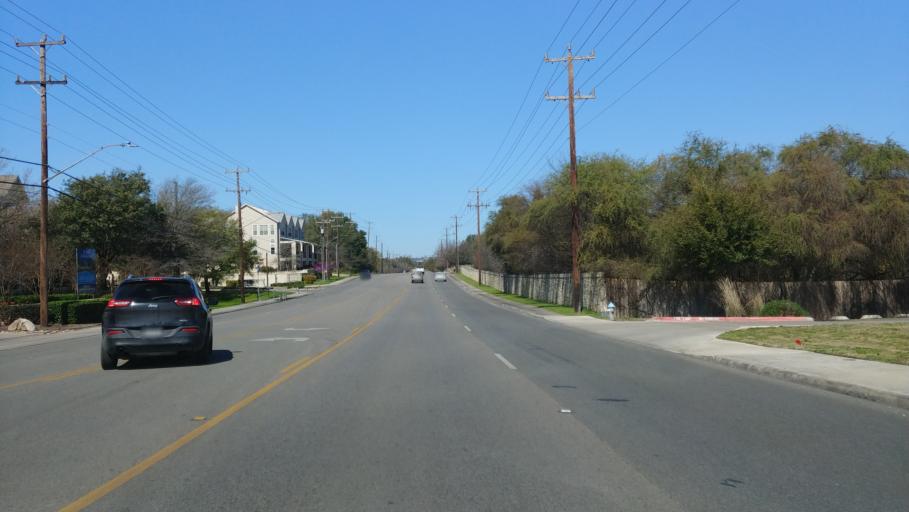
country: US
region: Texas
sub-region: Bexar County
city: Shavano Park
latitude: 29.5653
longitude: -98.5590
